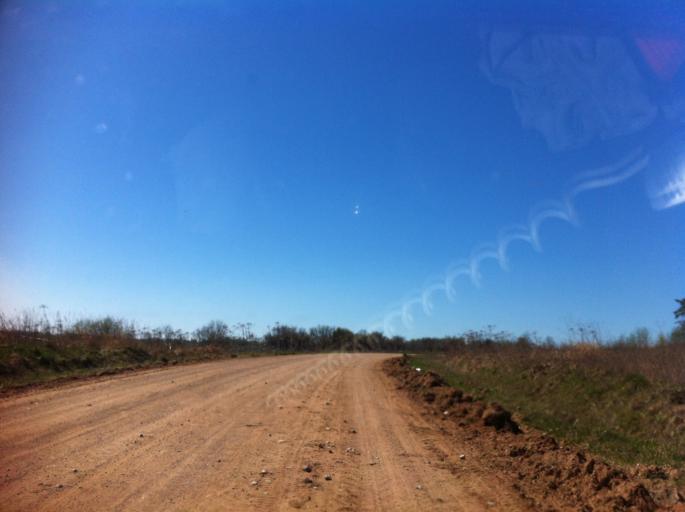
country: RU
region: Pskov
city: Izborsk
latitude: 57.8028
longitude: 27.9718
